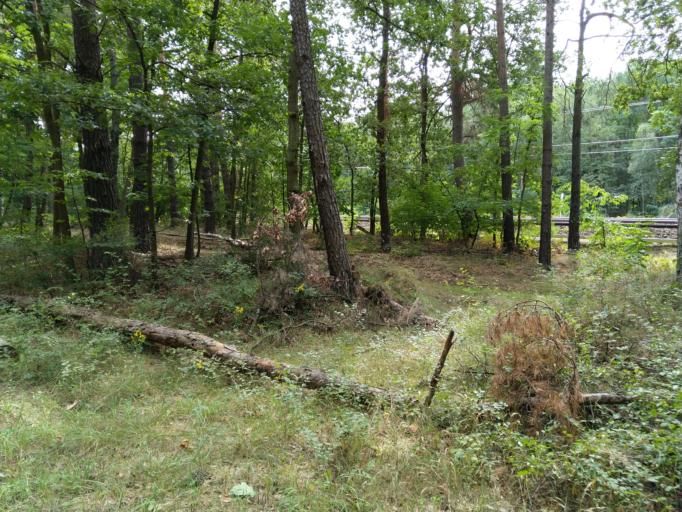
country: DE
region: Berlin
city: Rahnsdorf
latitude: 52.4500
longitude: 13.7062
